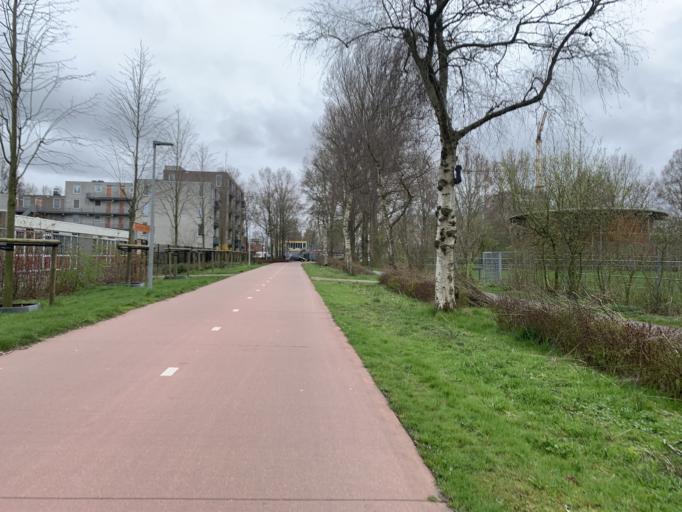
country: NL
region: Groningen
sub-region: Gemeente Groningen
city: Korrewegwijk
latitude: 53.2328
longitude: 6.5466
